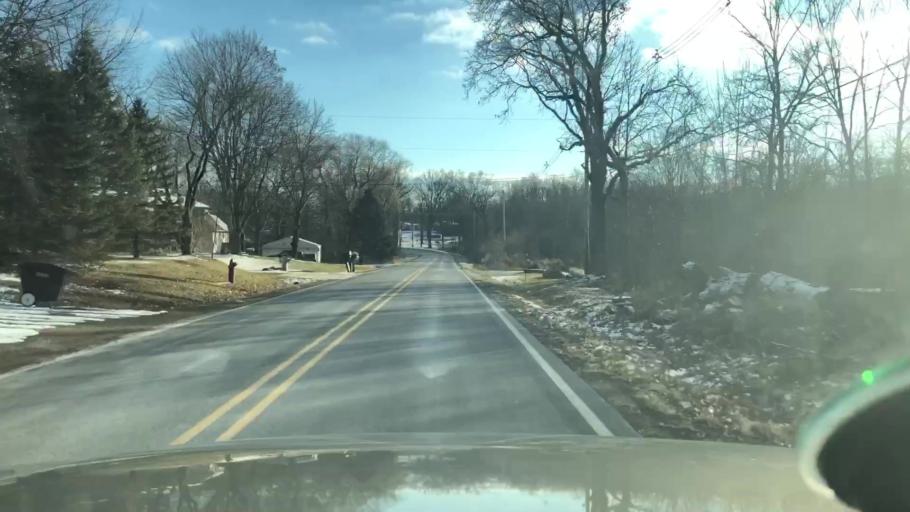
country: US
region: Michigan
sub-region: Jackson County
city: Vandercook Lake
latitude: 42.1632
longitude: -84.4525
